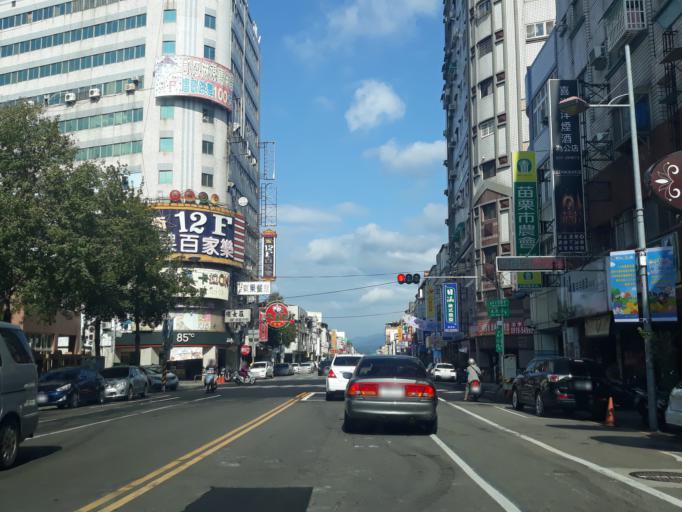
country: TW
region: Taiwan
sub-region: Miaoli
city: Miaoli
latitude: 24.5714
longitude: 120.8295
